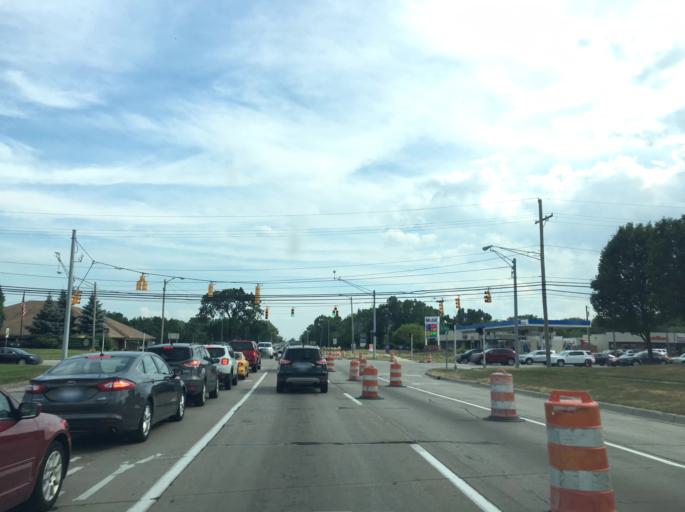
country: US
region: Michigan
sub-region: Macomb County
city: Fraser
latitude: 42.5528
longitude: -82.9897
